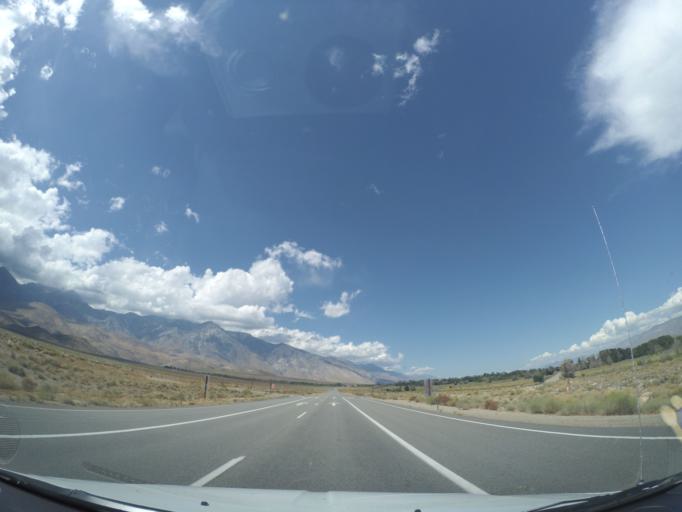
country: US
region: California
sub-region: Inyo County
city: Lone Pine
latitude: 36.8226
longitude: -118.2157
